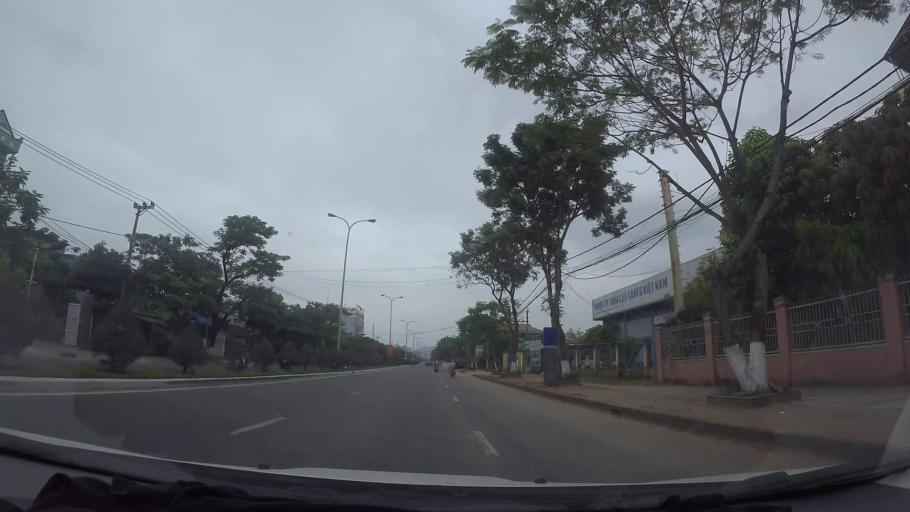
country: VN
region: Da Nang
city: Lien Chieu
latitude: 16.0901
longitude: 108.1429
